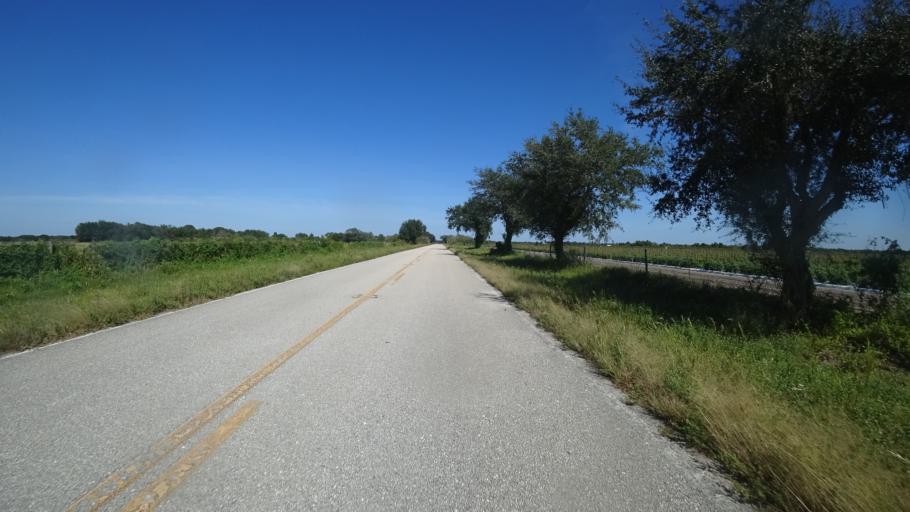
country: US
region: Florida
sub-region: DeSoto County
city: Arcadia
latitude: 27.2769
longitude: -82.0562
